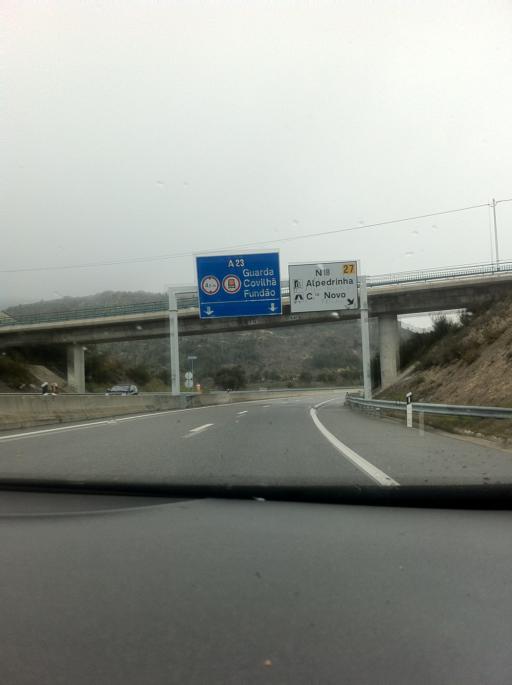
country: PT
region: Castelo Branco
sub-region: Concelho do Fundao
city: Fundao
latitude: 40.0717
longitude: -7.4819
